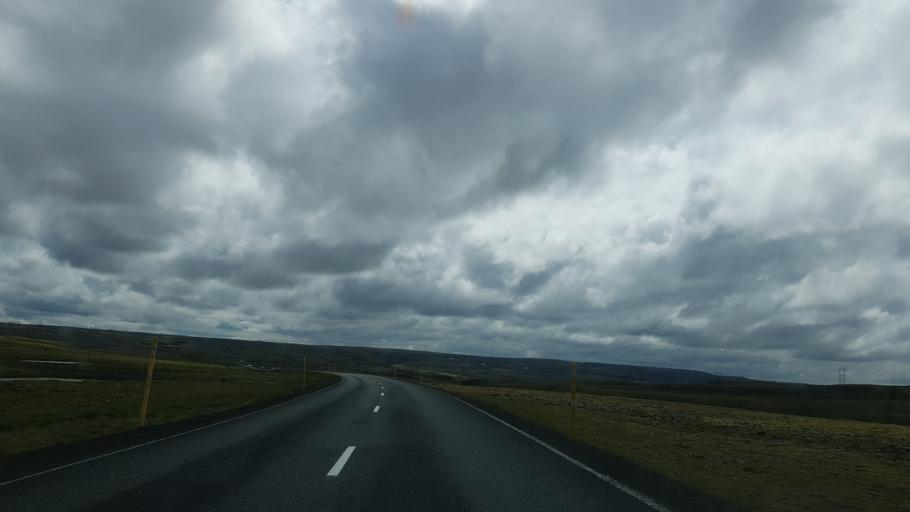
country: IS
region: West
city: Borgarnes
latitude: 64.9592
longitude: -21.0609
